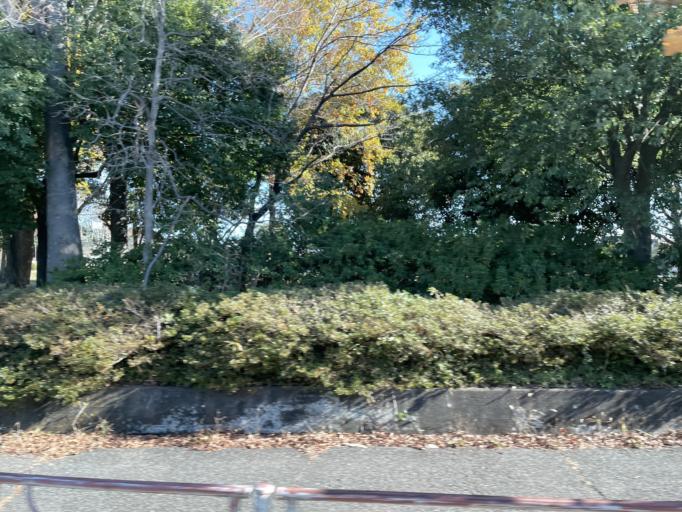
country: JP
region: Saitama
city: Kukichuo
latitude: 36.0714
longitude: 139.6951
